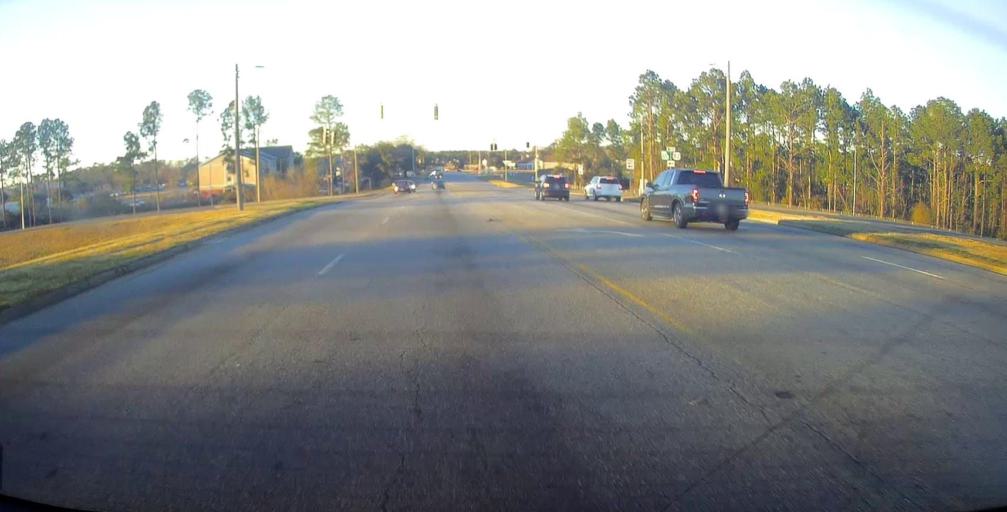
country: US
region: Georgia
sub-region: Dougherty County
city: Albany
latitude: 31.6189
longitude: -84.2043
